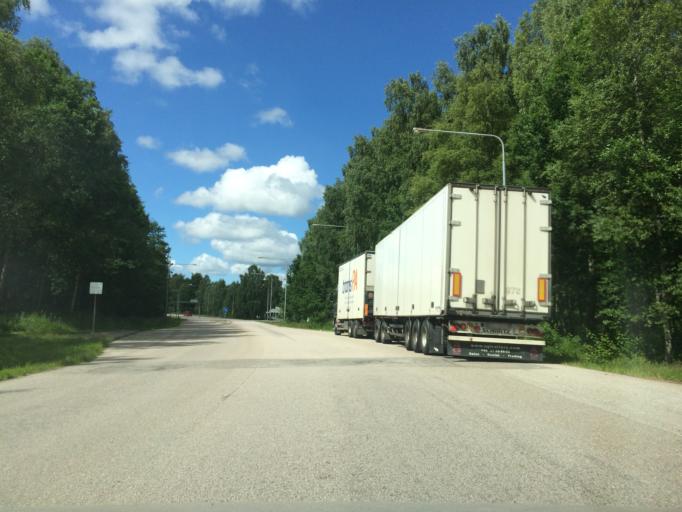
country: SE
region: Vaestra Goetaland
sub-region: Trollhattan
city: Trollhattan
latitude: 58.2950
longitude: 12.3113
